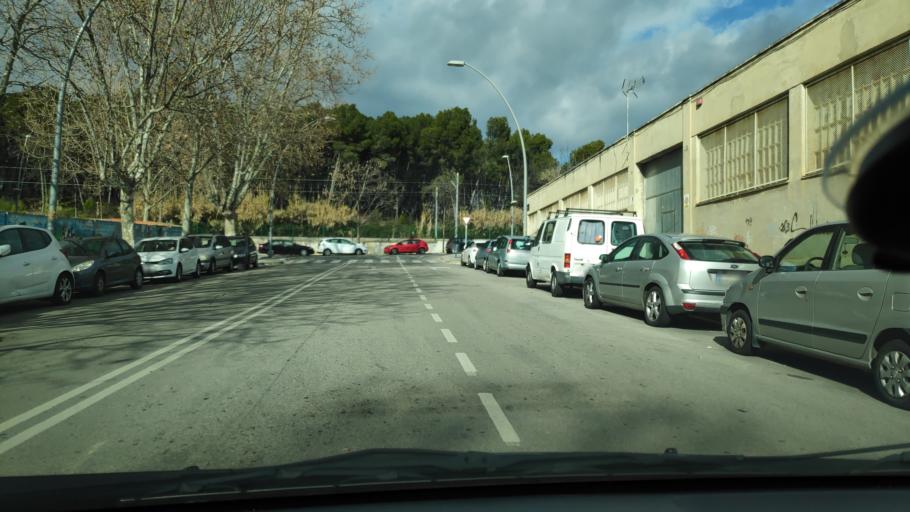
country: ES
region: Catalonia
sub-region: Provincia de Barcelona
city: Terrassa
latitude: 41.5648
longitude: 1.9960
